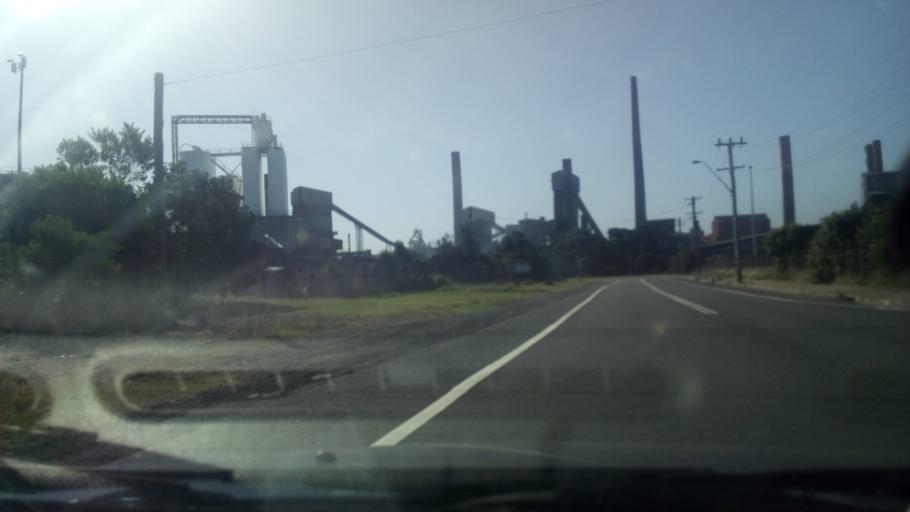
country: AU
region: New South Wales
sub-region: Wollongong
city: Port Kembla
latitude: -34.4700
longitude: 150.8983
